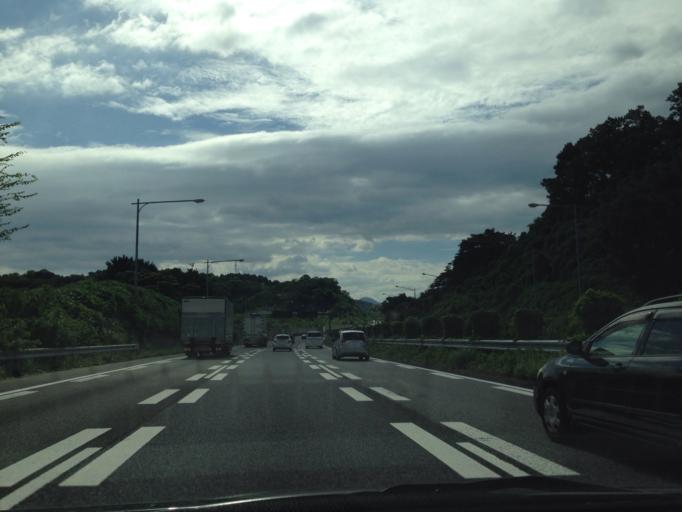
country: JP
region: Kanagawa
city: Hadano
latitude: 35.3411
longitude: 139.1988
